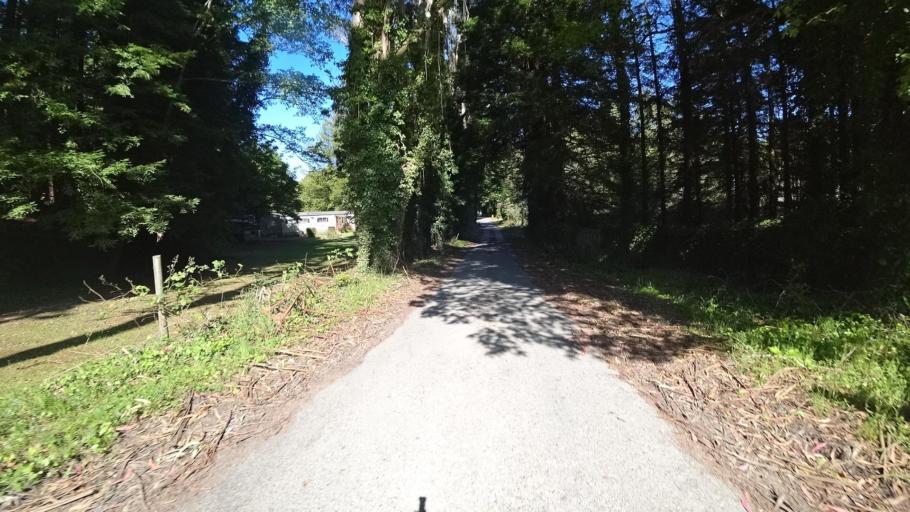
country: US
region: California
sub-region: Humboldt County
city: Rio Dell
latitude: 40.5285
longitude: -124.1662
